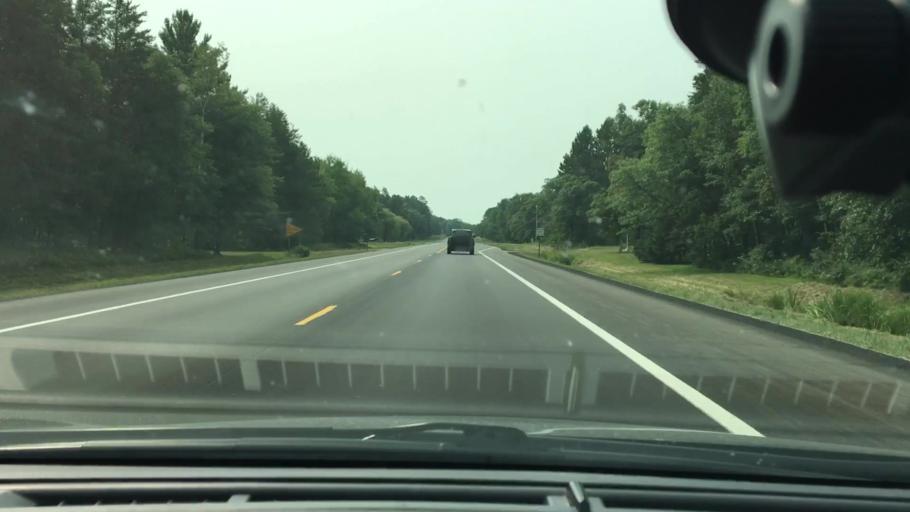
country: US
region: Minnesota
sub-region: Crow Wing County
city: Brainerd
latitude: 46.4444
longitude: -94.1718
